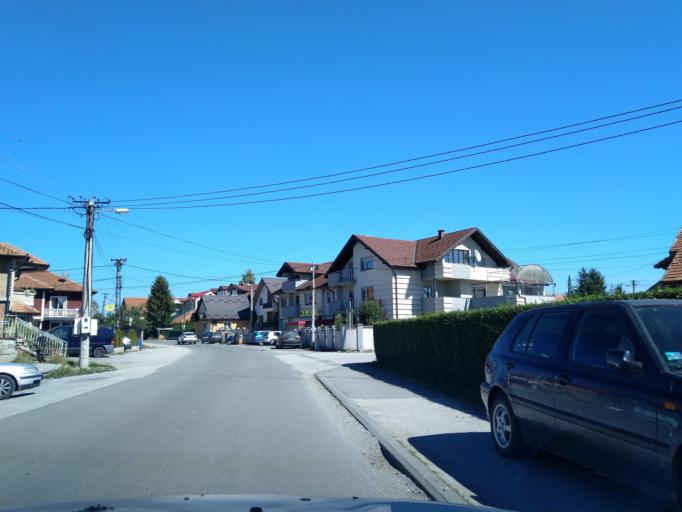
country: RS
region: Central Serbia
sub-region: Zlatiborski Okrug
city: Sjenica
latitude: 43.2738
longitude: 20.0106
